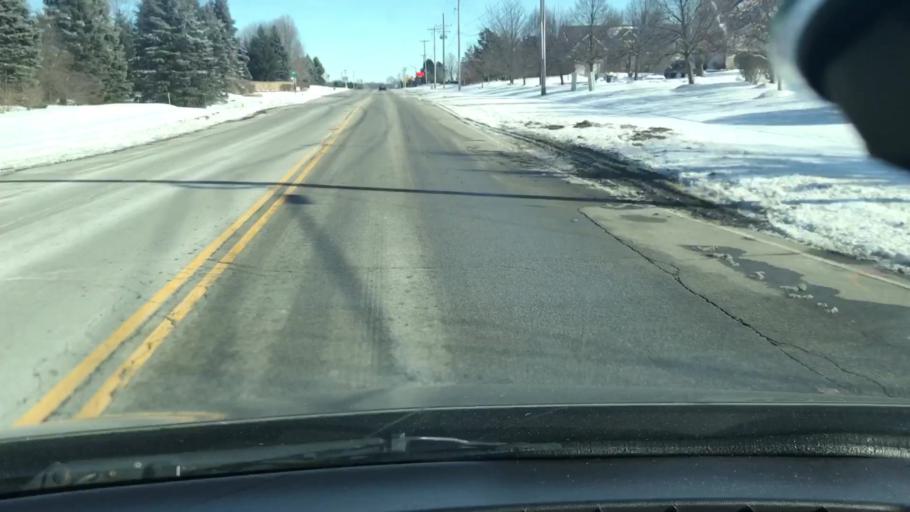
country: US
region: Indiana
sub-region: Hamilton County
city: Carmel
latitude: 39.9712
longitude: -86.0752
